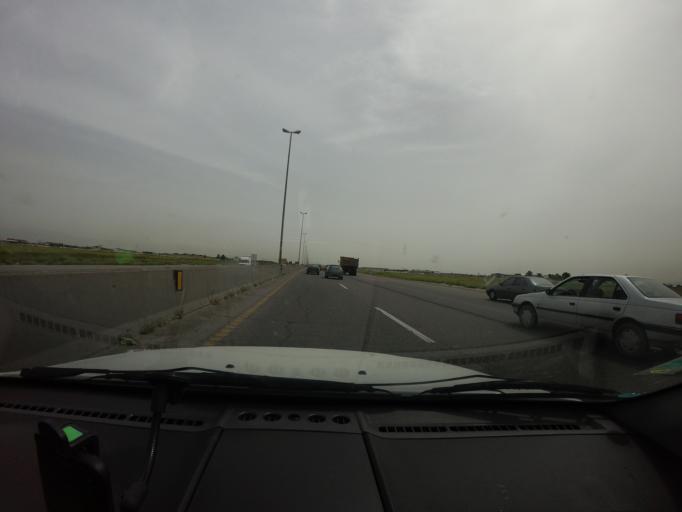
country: IR
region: Tehran
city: Robat Karim
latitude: 35.5355
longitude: 51.1021
